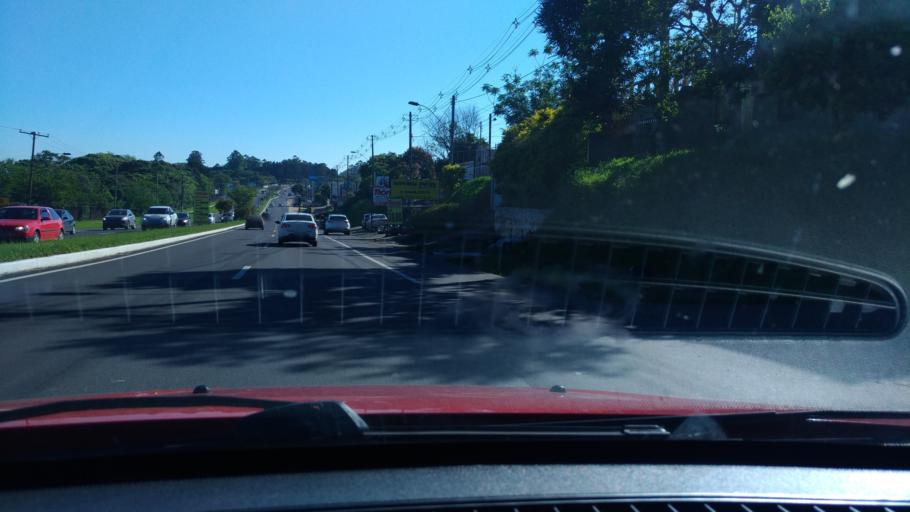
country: BR
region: Rio Grande do Sul
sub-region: Viamao
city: Viamao
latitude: -30.0828
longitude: -51.0535
